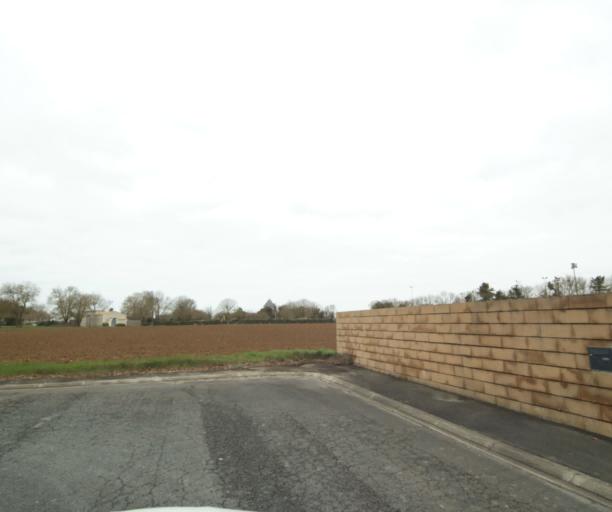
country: FR
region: Poitou-Charentes
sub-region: Departement de la Charente-Maritime
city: Lagord
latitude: 46.1943
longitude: -1.1546
